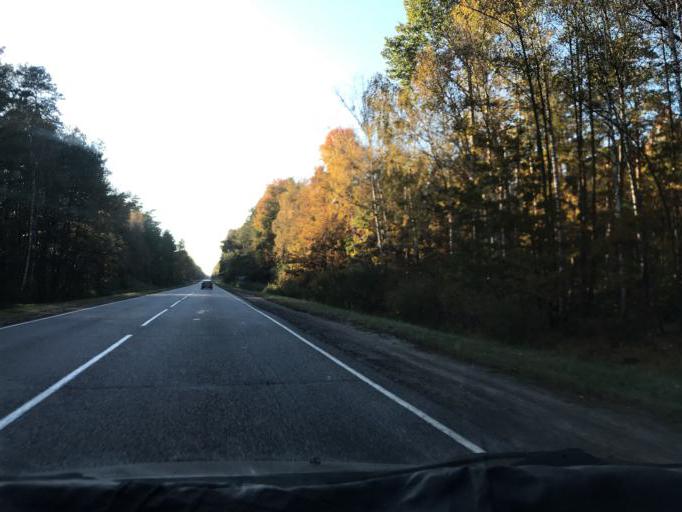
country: BY
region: Gomel
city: Zhytkavichy
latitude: 52.2736
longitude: 28.1199
